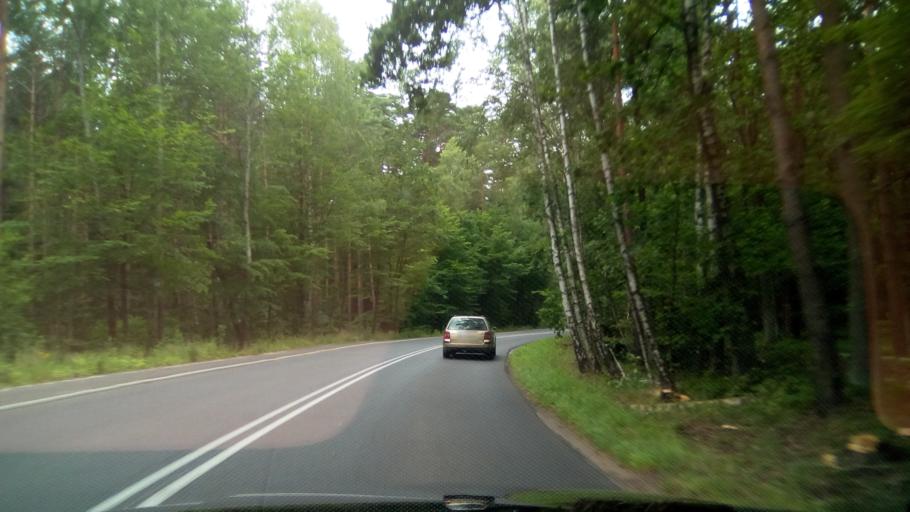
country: PL
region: Greater Poland Voivodeship
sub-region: Powiat gnieznienski
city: Czerniejewo
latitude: 52.4412
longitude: 17.4183
